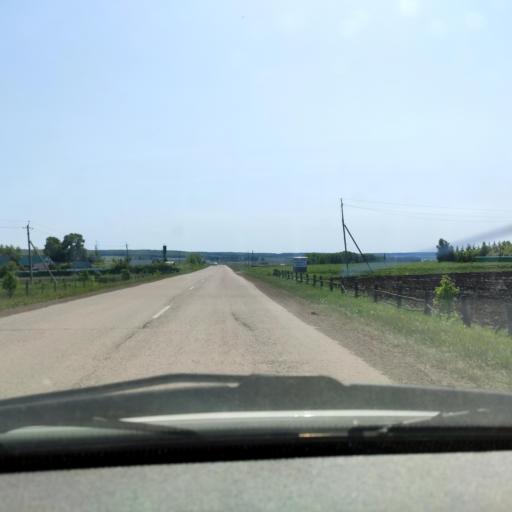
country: RU
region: Bashkortostan
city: Avdon
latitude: 54.5038
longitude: 55.6199
